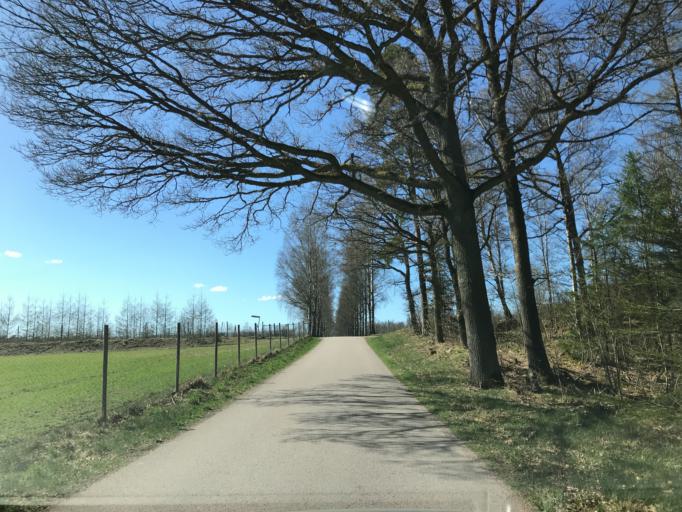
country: SE
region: Skane
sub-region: Klippans Kommun
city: Ljungbyhed
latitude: 56.0701
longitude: 13.2732
